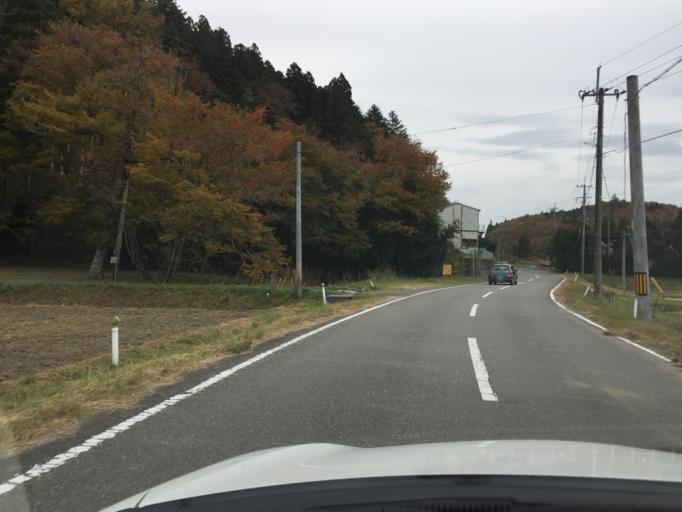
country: JP
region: Fukushima
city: Iwaki
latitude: 37.1787
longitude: 140.7226
